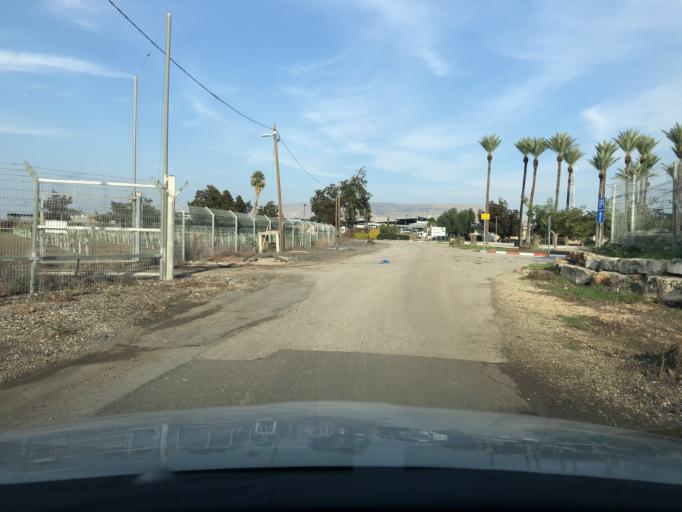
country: IL
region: Northern District
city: Yavne'el
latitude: 32.6636
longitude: 35.5802
